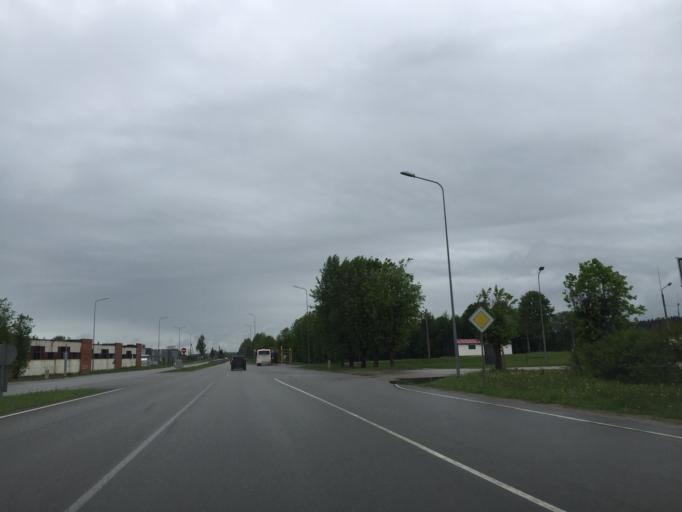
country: LV
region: Ogre
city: Ogre
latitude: 56.7936
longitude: 24.6313
